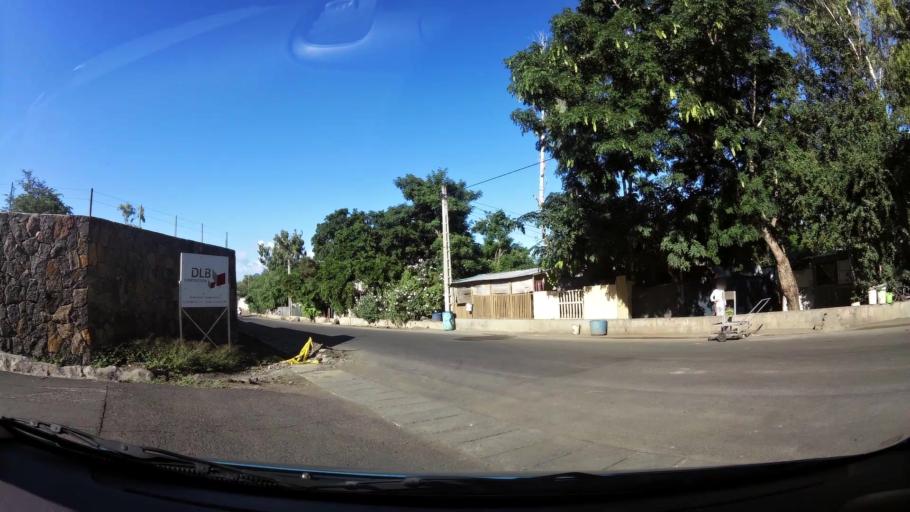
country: MU
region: Black River
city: Grande Riviere Noire
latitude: -20.3541
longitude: 57.3662
